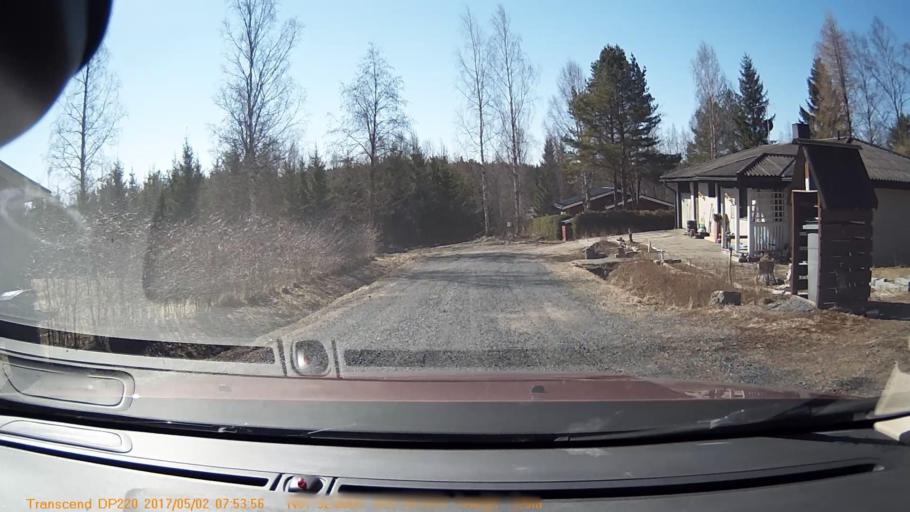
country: FI
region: Pirkanmaa
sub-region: Tampere
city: Kuru
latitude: 61.8781
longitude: 23.7120
